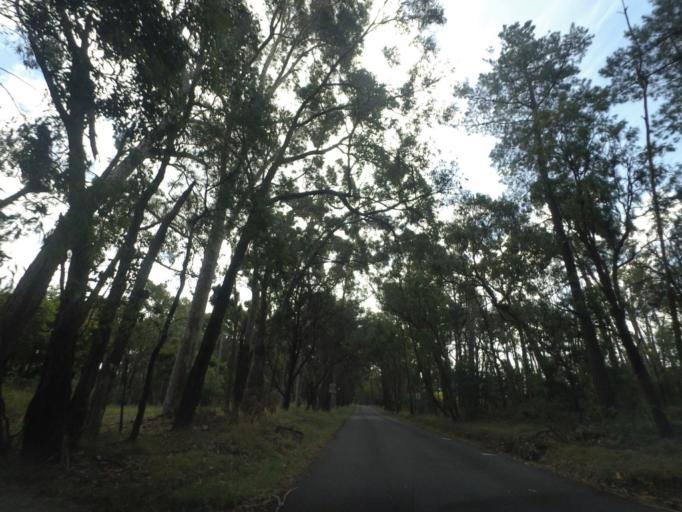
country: AU
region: Victoria
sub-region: Yarra Ranges
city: Mount Evelyn
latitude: -37.7862
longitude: 145.3530
